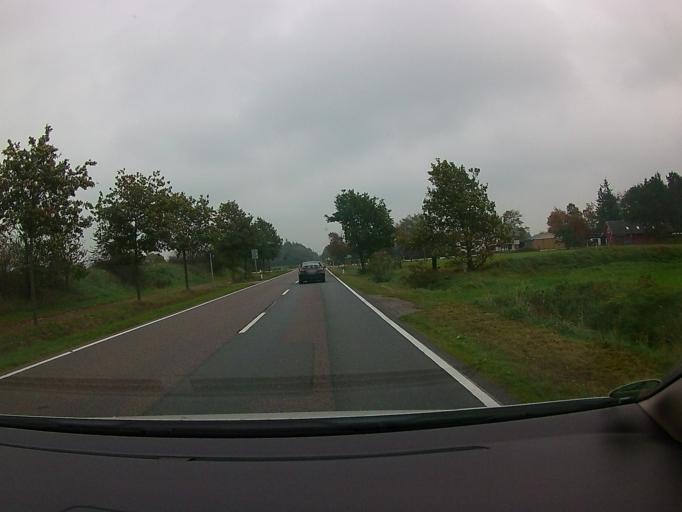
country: DE
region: Schleswig-Holstein
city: Goldebek
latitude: 54.6761
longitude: 9.1425
